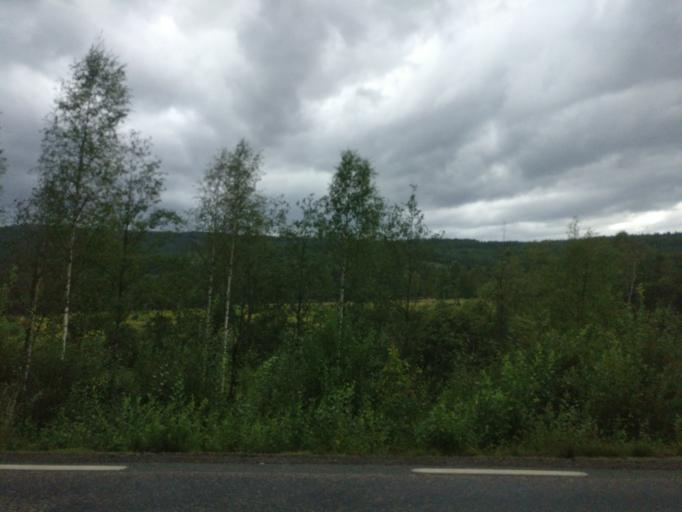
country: SE
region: Vaermland
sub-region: Torsby Kommun
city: Torsby
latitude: 60.6254
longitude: 13.0295
